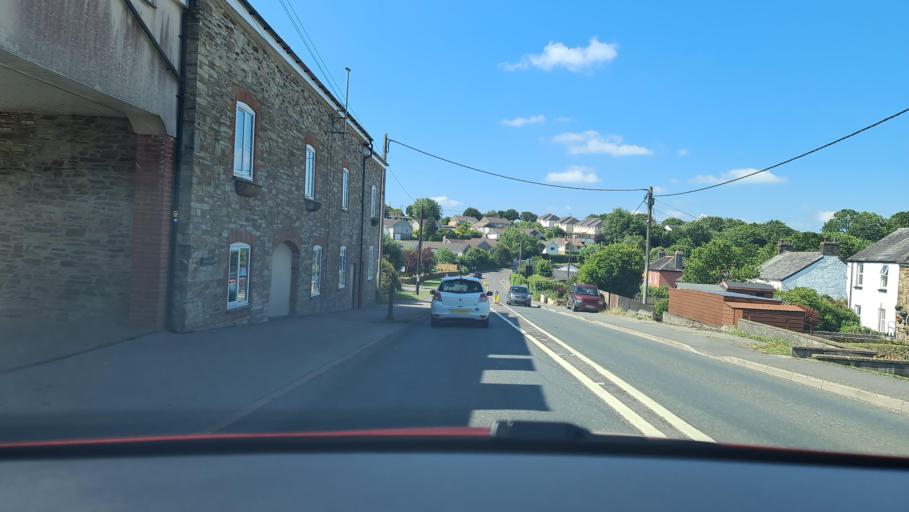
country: GB
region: England
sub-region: Cornwall
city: Liskeard
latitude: 50.4432
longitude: -4.5614
